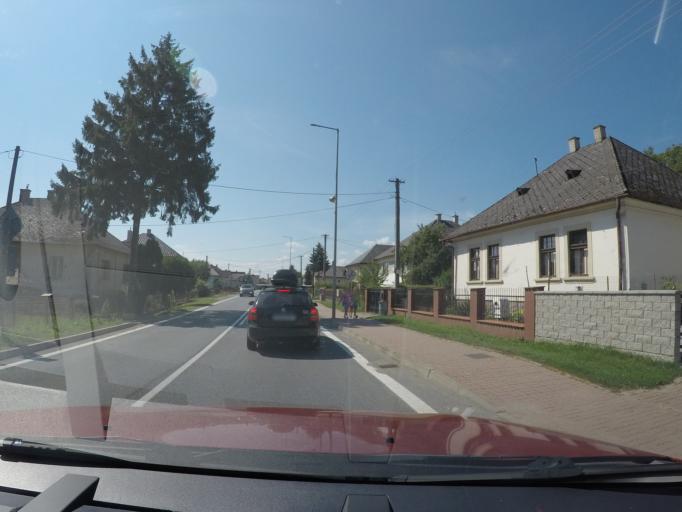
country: SK
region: Presovsky
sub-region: Okres Presov
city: Presov
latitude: 48.9249
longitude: 21.2411
